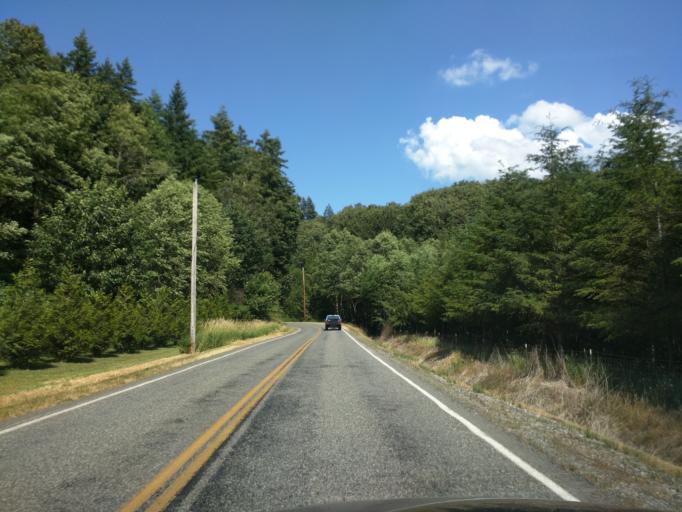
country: US
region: Washington
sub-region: Whatcom County
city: Peaceful Valley
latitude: 48.9625
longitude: -122.1735
